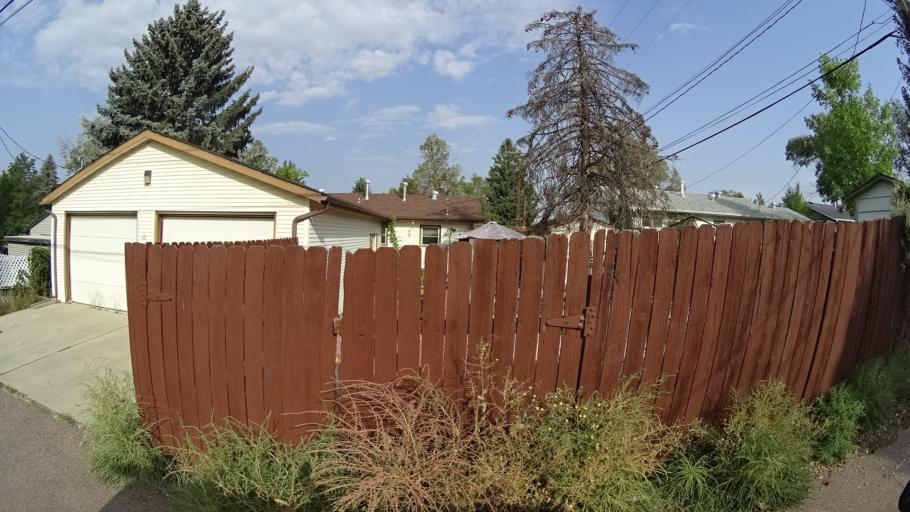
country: US
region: Colorado
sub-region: El Paso County
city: Colorado Springs
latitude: 38.8525
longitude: -104.7785
